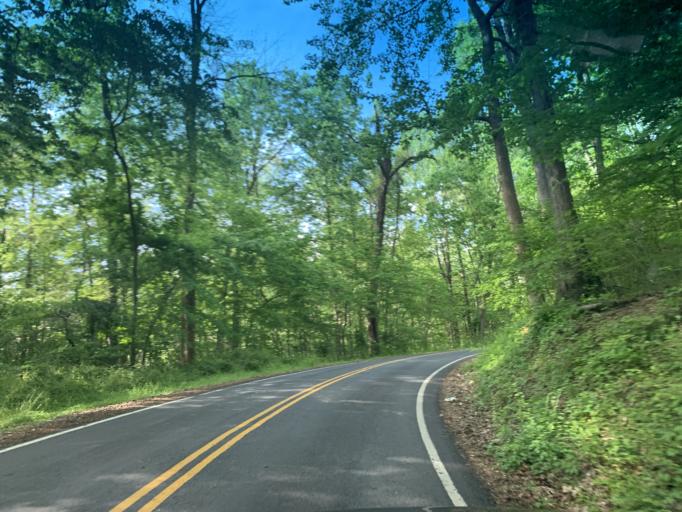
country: US
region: Maryland
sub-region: Cecil County
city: Rising Sun
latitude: 39.6888
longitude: -76.2022
